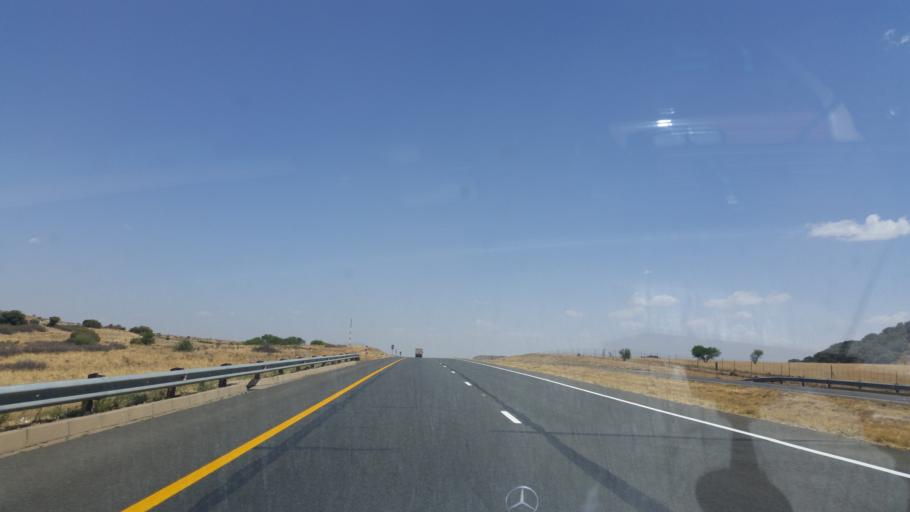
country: ZA
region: Orange Free State
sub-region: Lejweleputswa District Municipality
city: Brandfort
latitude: -28.9276
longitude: 26.4306
